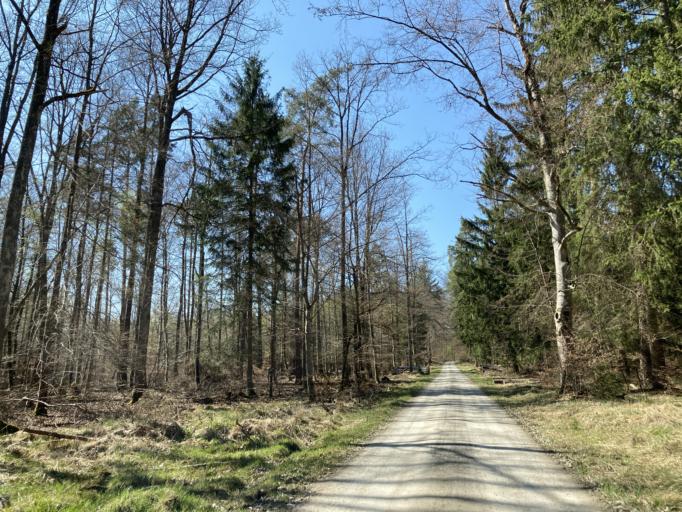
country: DE
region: Baden-Wuerttemberg
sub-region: Regierungsbezirk Stuttgart
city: Altdorf
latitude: 48.5716
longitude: 9.0071
